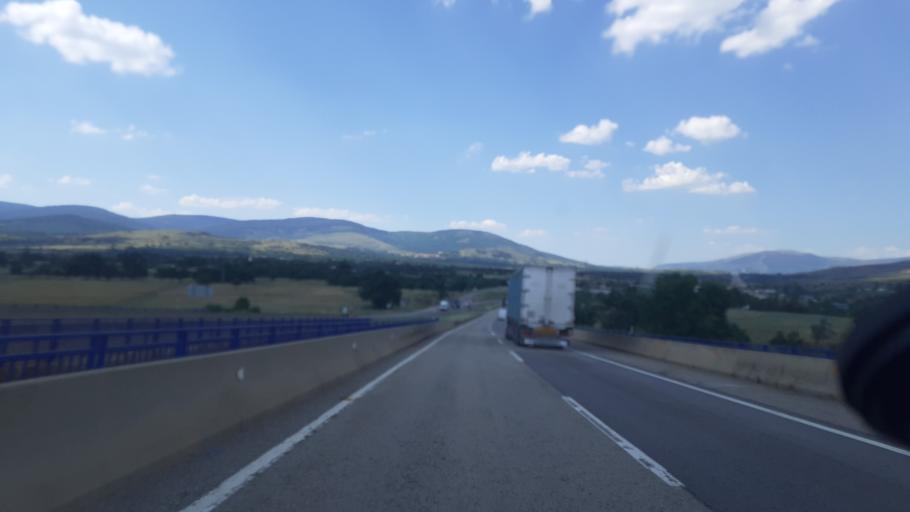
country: ES
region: Madrid
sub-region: Provincia de Madrid
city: Buitrago del Lozoya
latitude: 40.9932
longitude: -3.6423
